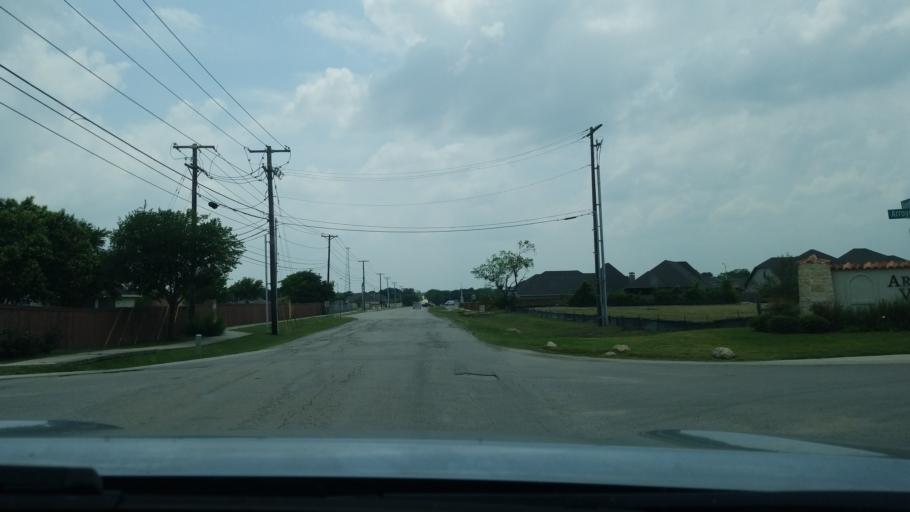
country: US
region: Texas
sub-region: Comal County
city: New Braunfels
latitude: 29.7522
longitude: -98.0704
